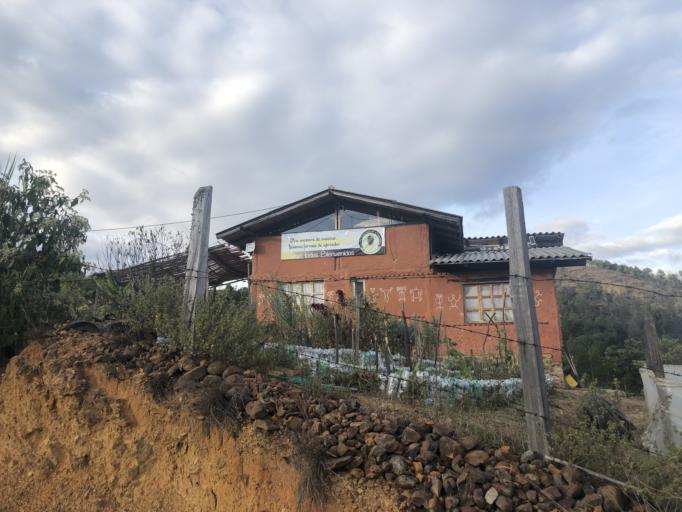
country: CO
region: Boyaca
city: Raquira
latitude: 5.5755
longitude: -73.6594
